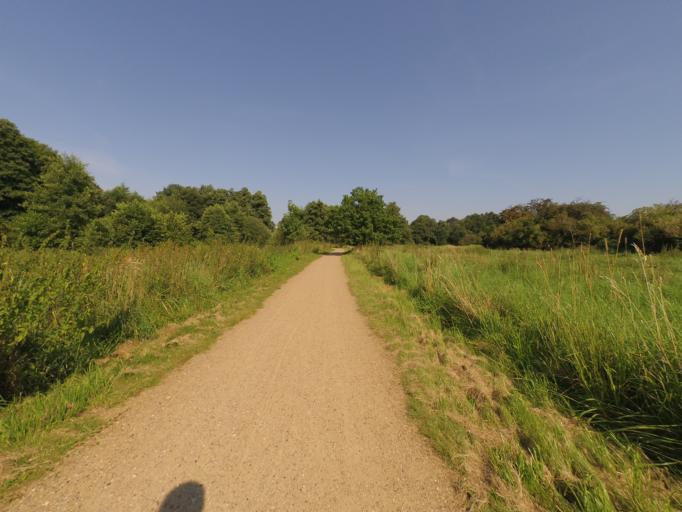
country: DE
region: Schleswig-Holstein
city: Oststeinbek
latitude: 53.5133
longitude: 10.1306
